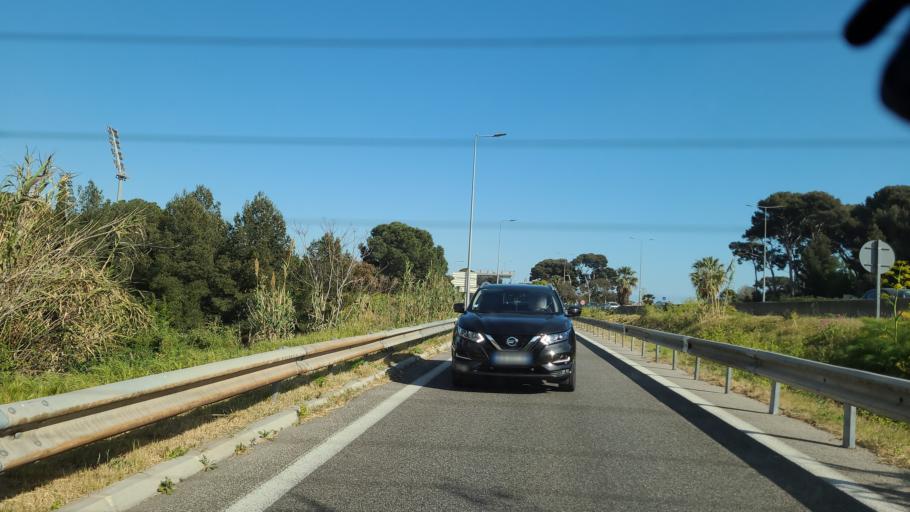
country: FR
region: Provence-Alpes-Cote d'Azur
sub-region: Departement du Var
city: La Seyne-sur-Mer
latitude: 43.1254
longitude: 5.8999
